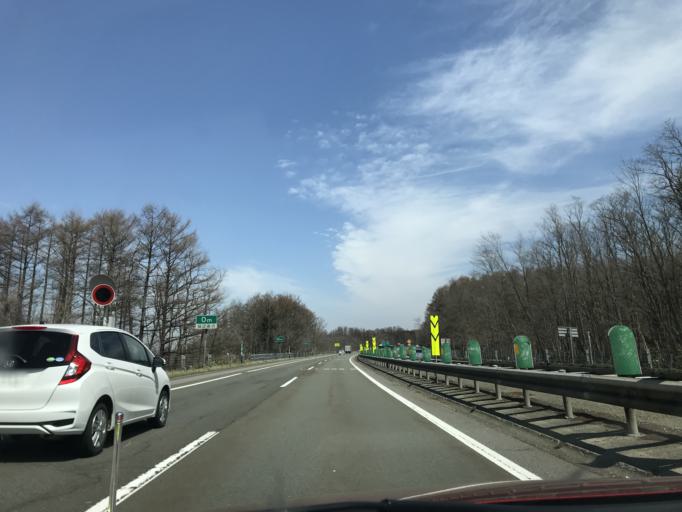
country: JP
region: Hokkaido
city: Bibai
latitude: 43.2772
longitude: 141.8511
